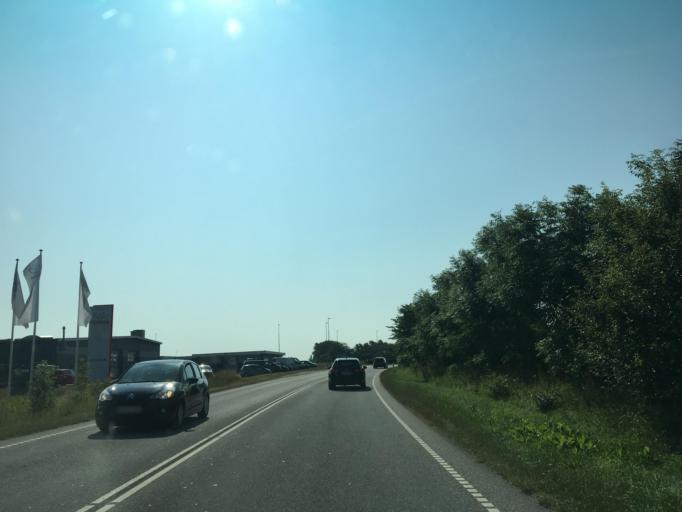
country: DK
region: North Denmark
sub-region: Thisted Kommune
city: Thisted
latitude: 56.9368
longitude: 8.6438
